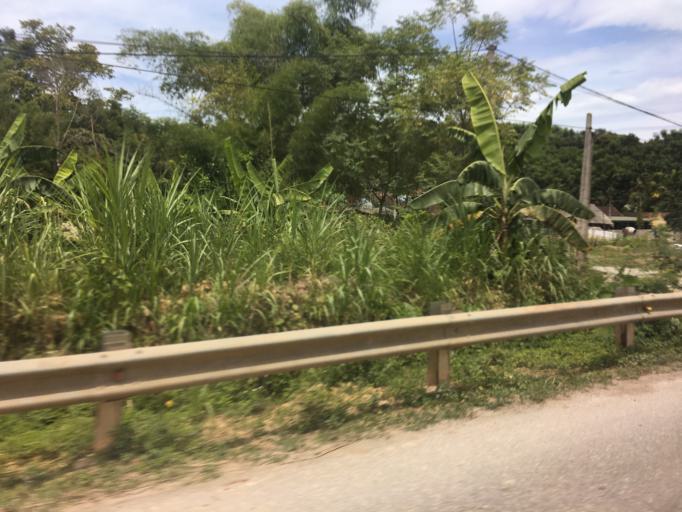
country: VN
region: Ha Tinh
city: Huong Khe
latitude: 18.2651
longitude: 105.6459
